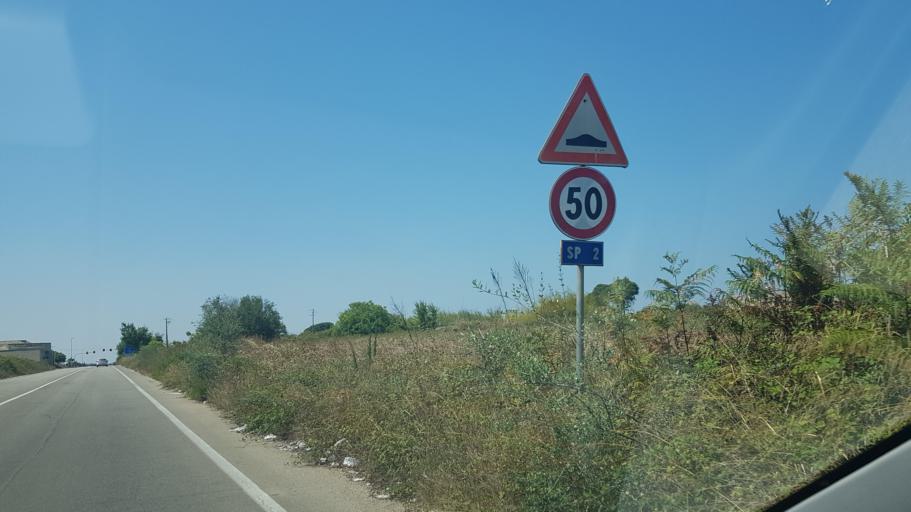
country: IT
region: Apulia
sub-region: Provincia di Lecce
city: Vernole
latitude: 40.2905
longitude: 18.3077
